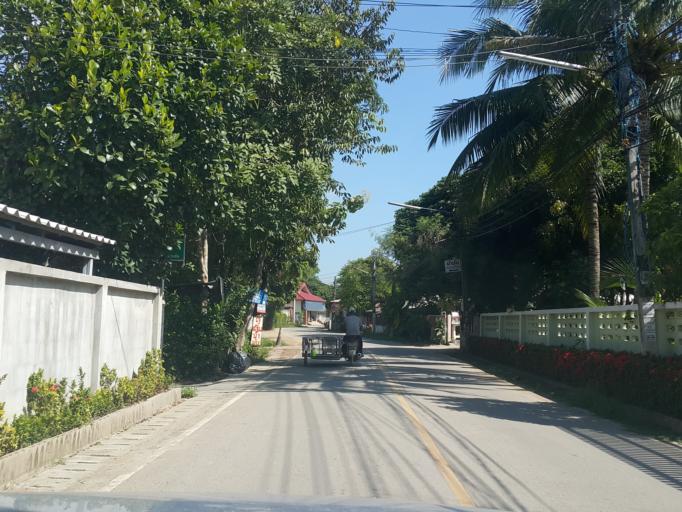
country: TH
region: Chiang Mai
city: Saraphi
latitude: 18.7508
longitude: 99.0513
